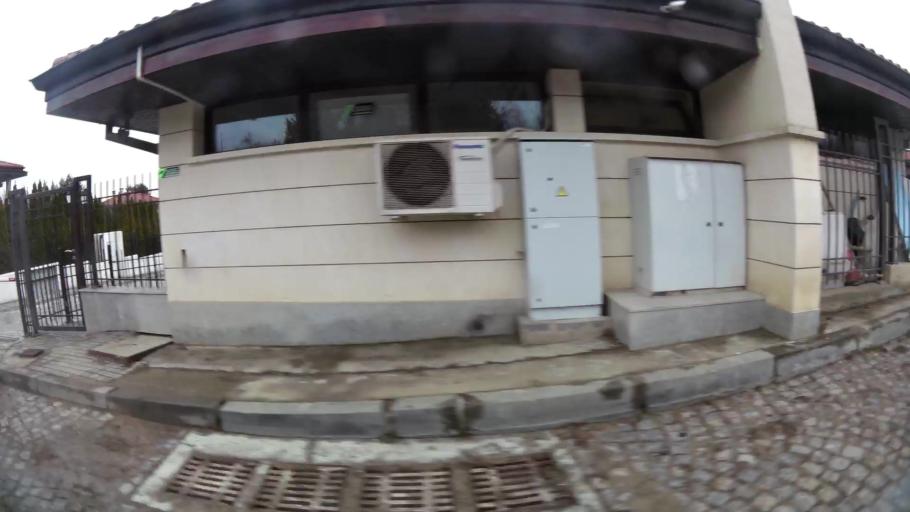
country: BG
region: Sofia-Capital
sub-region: Stolichna Obshtina
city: Sofia
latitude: 42.6148
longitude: 23.3761
